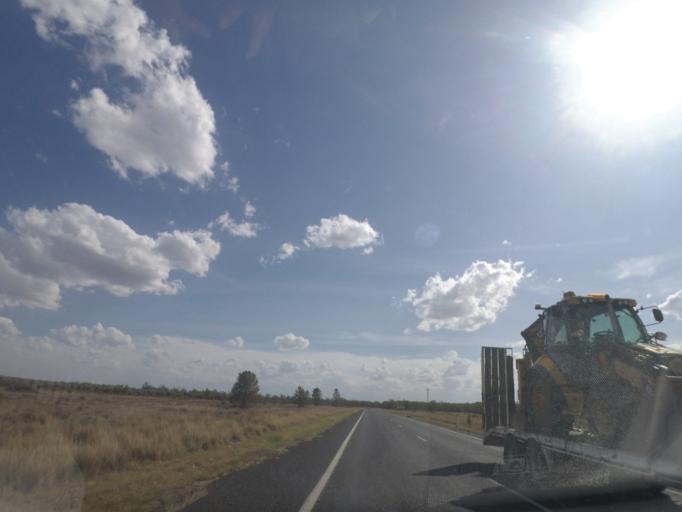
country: AU
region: New South Wales
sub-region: Moree Plains
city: Boggabilla
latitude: -28.5310
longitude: 150.8971
